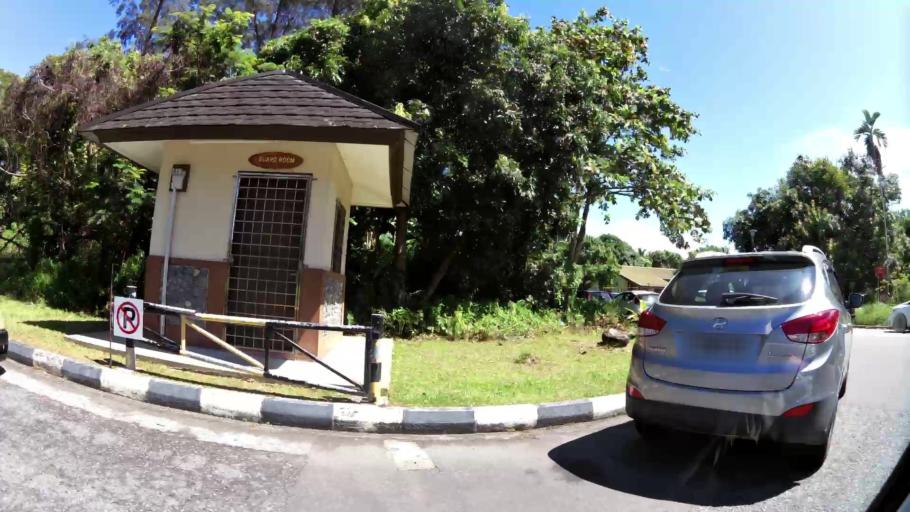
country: BN
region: Brunei and Muara
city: Bandar Seri Begawan
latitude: 5.0359
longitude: 115.0787
